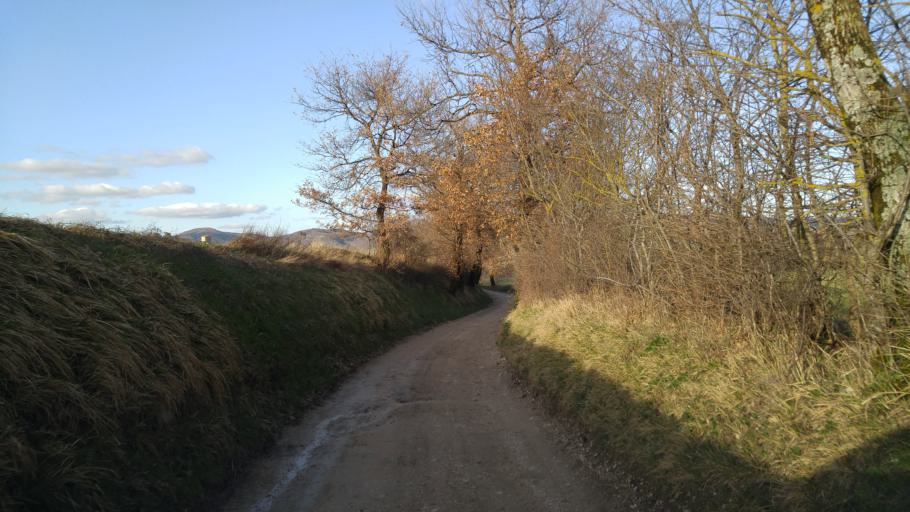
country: IT
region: The Marches
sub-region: Provincia di Pesaro e Urbino
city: Cagli
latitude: 43.5353
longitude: 12.6937
